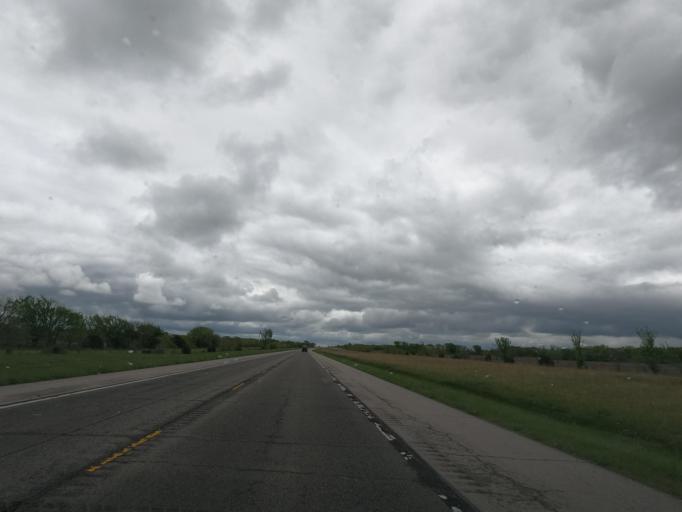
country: US
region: Kansas
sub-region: Montgomery County
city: Cherryvale
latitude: 37.3434
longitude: -95.4294
